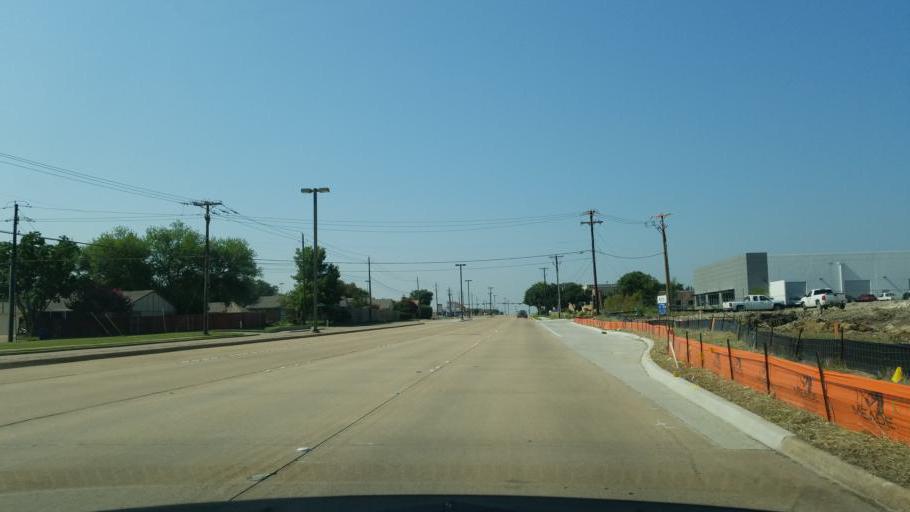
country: US
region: Texas
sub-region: Collin County
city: Allen
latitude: 33.0905
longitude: -96.6691
